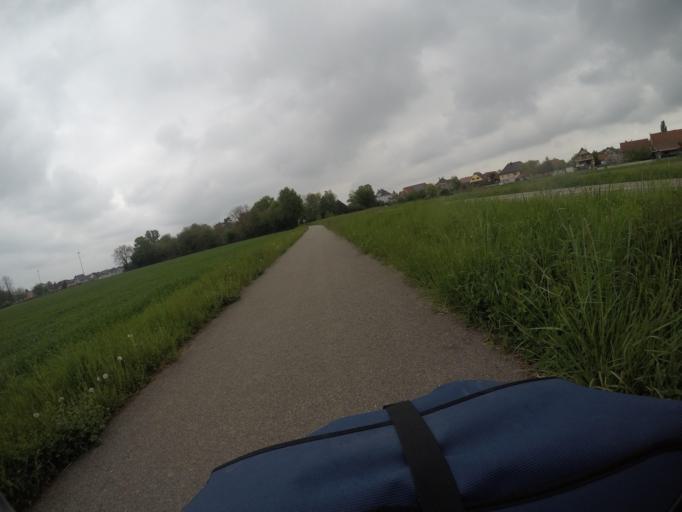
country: FR
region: Alsace
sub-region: Departement du Bas-Rhin
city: Soufflenheim
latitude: 48.8107
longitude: 8.0064
